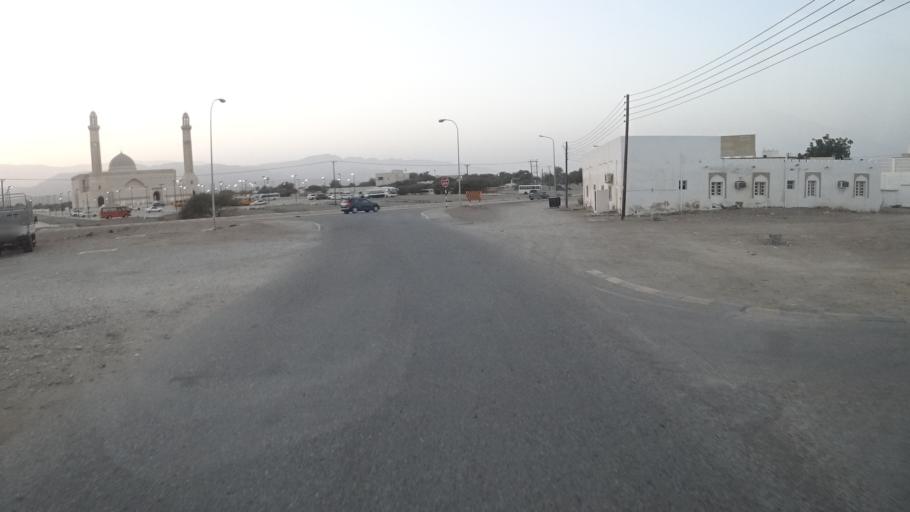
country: OM
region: Ash Sharqiyah
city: Sur
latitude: 22.5438
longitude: 59.4837
